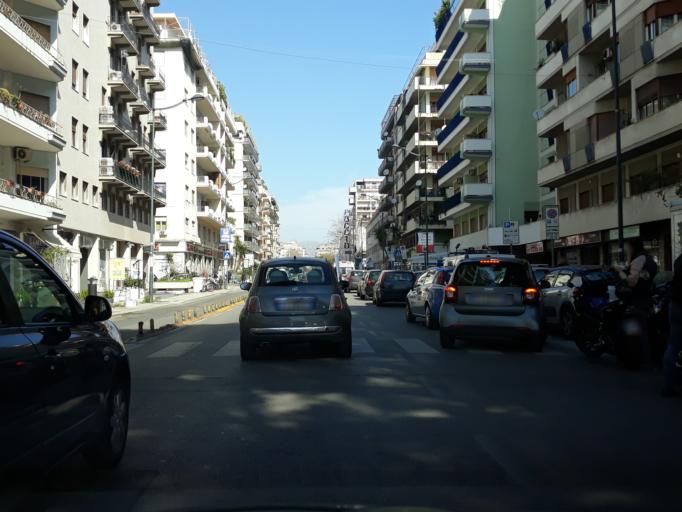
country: IT
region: Sicily
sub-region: Palermo
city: Palermo
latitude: 38.1355
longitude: 13.3515
